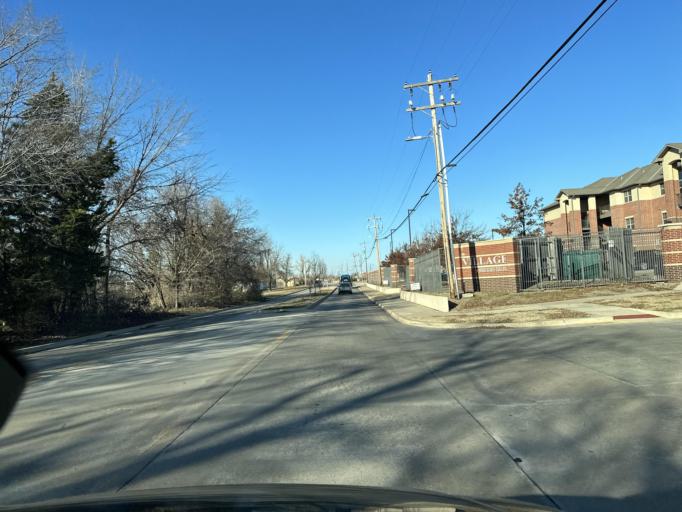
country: US
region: Oklahoma
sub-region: Oklahoma County
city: Midwest City
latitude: 35.4462
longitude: -97.4164
